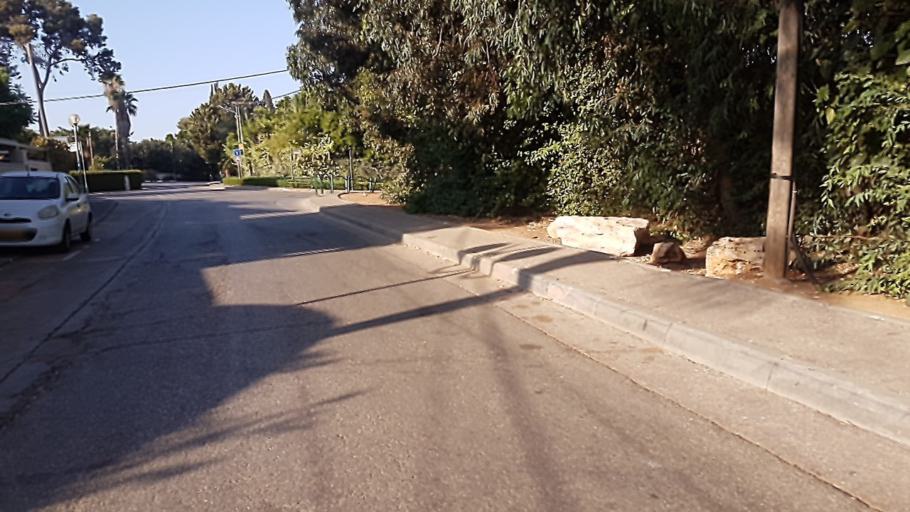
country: IL
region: Central District
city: Hod HaSharon
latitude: 32.1406
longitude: 34.9034
